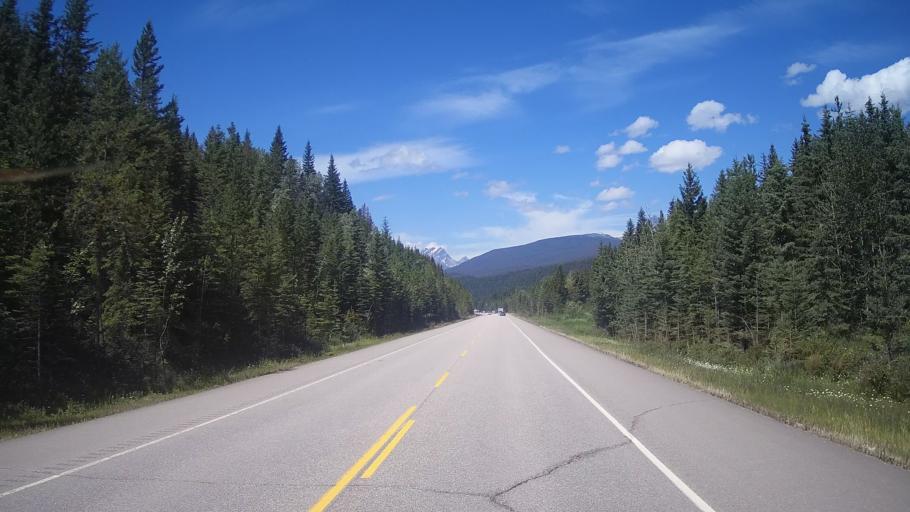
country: CA
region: Alberta
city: Jasper Park Lodge
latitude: 52.8786
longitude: -118.3460
